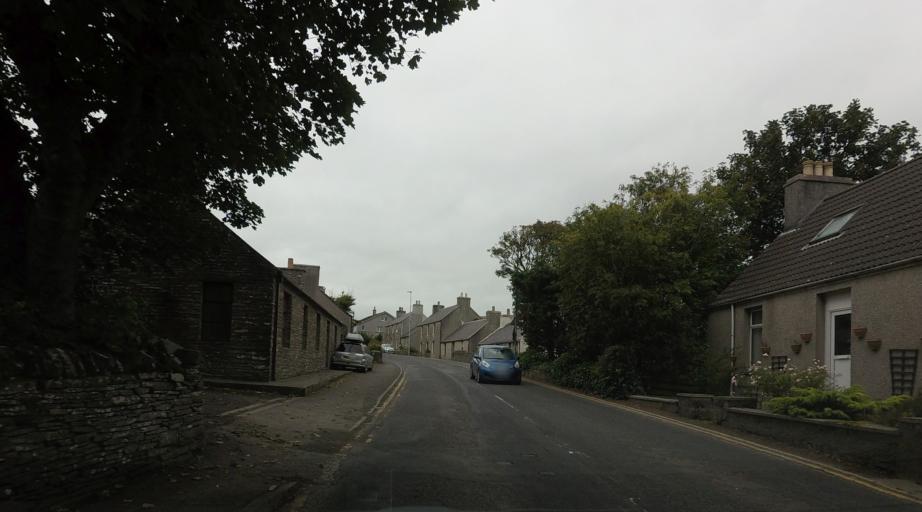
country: GB
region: Scotland
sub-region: Orkney Islands
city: Orkney
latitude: 59.0075
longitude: -3.1169
